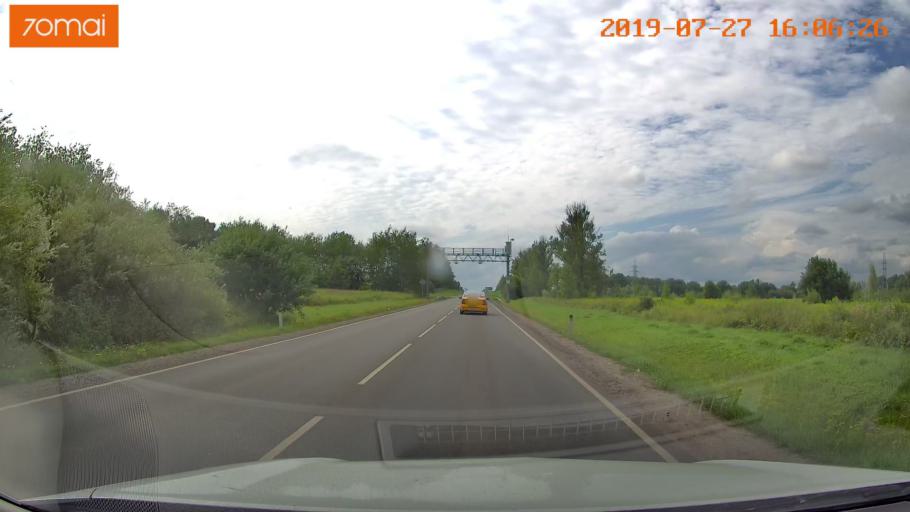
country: RU
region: Kaliningrad
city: Chernyakhovsk
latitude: 54.6340
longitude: 21.7772
